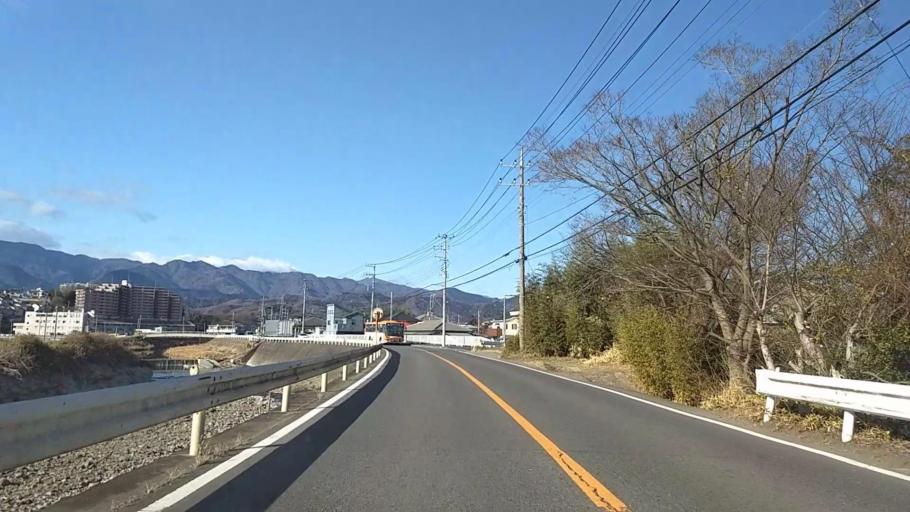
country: JP
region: Kanagawa
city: Atsugi
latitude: 35.4654
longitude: 139.3417
